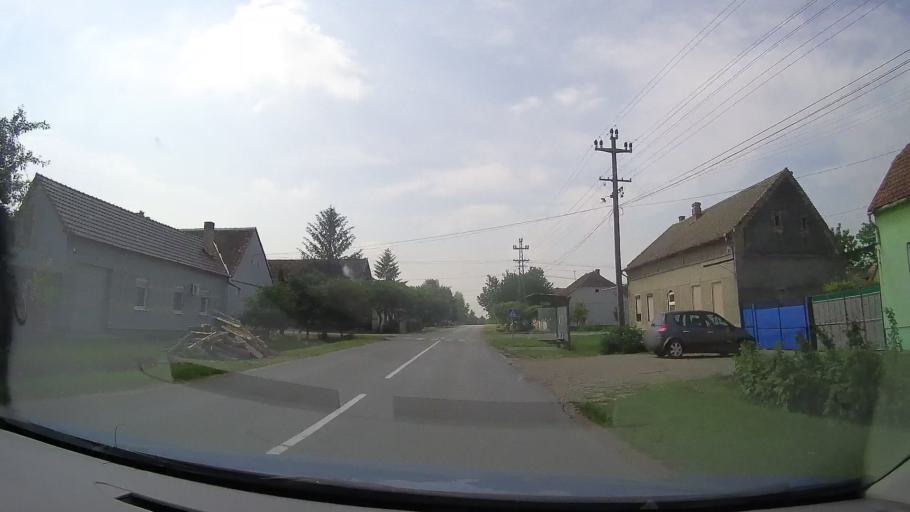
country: RS
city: Padina
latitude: 45.1239
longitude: 20.7220
